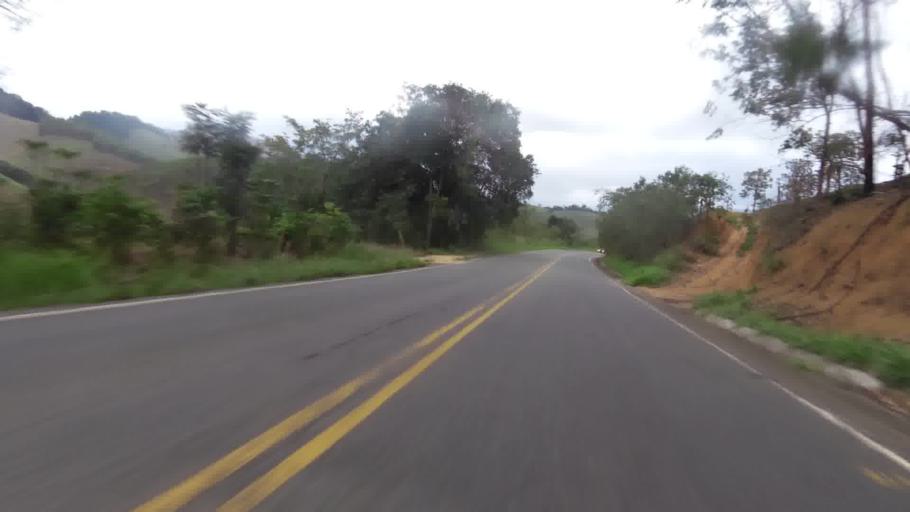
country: BR
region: Espirito Santo
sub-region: Alfredo Chaves
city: Alfredo Chaves
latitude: -20.6652
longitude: -40.7189
